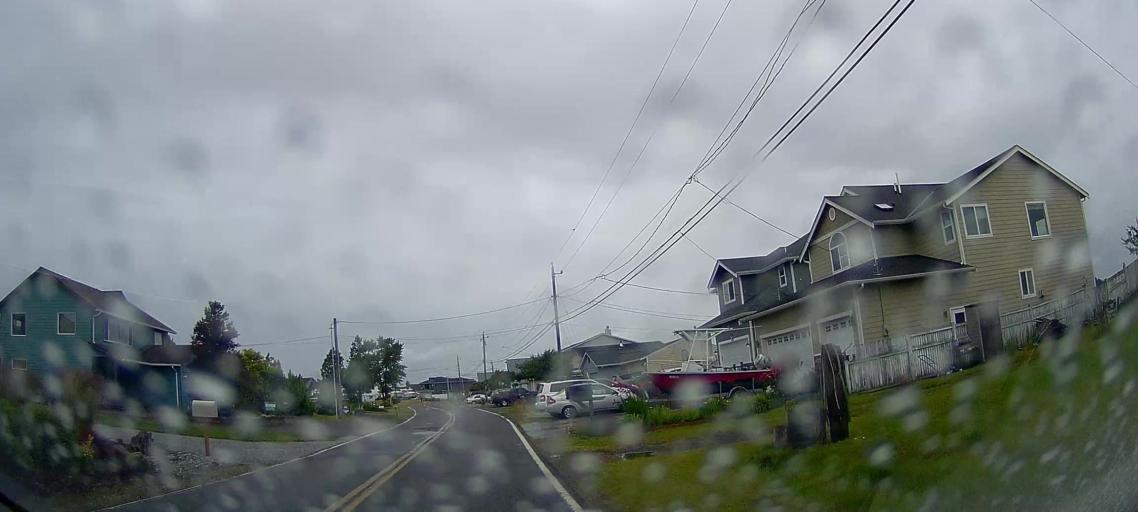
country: US
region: Washington
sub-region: Whatcom County
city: Marietta
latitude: 48.7939
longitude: -122.7047
